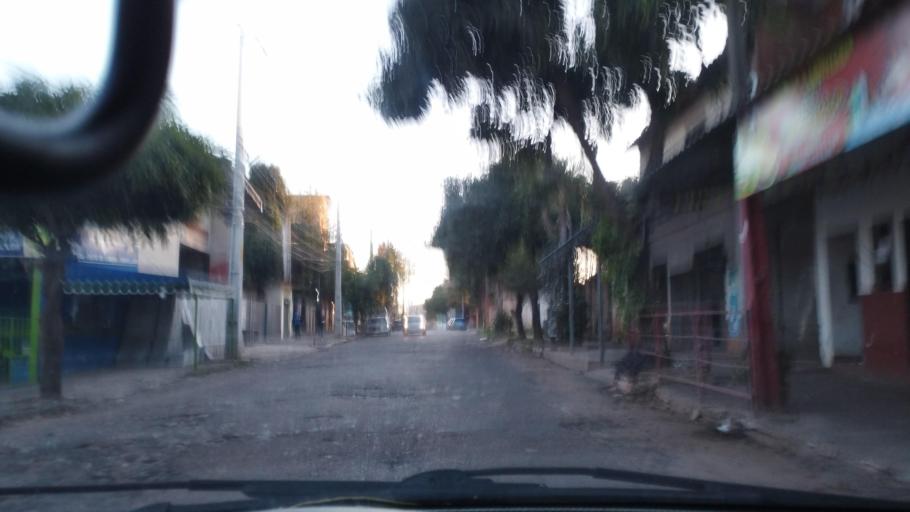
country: PY
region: Central
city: Fernando de la Mora
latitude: -25.3054
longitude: -57.5339
